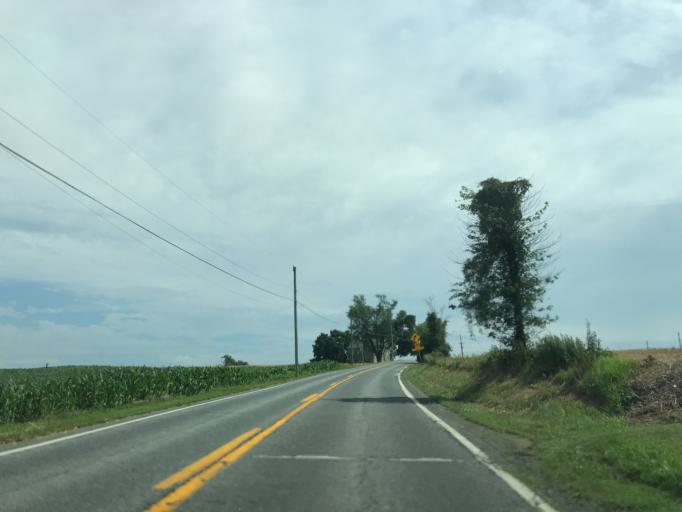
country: US
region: Pennsylvania
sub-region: York County
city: Susquehanna Trails
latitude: 39.6939
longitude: -76.3897
